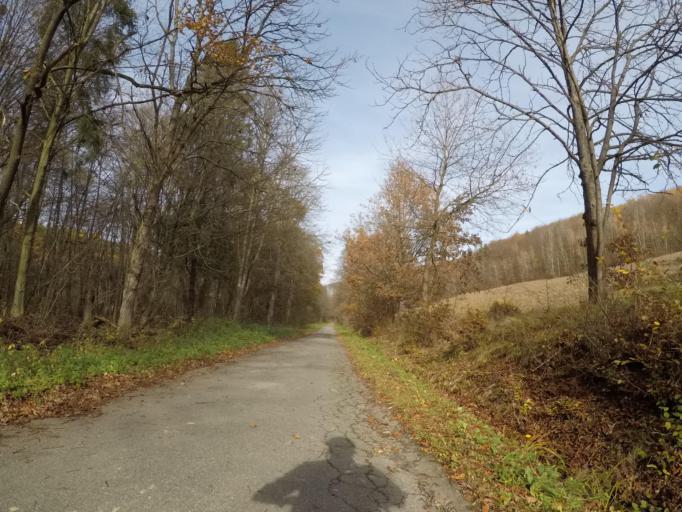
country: SK
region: Presovsky
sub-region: Okres Presov
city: Presov
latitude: 48.9686
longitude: 21.1927
